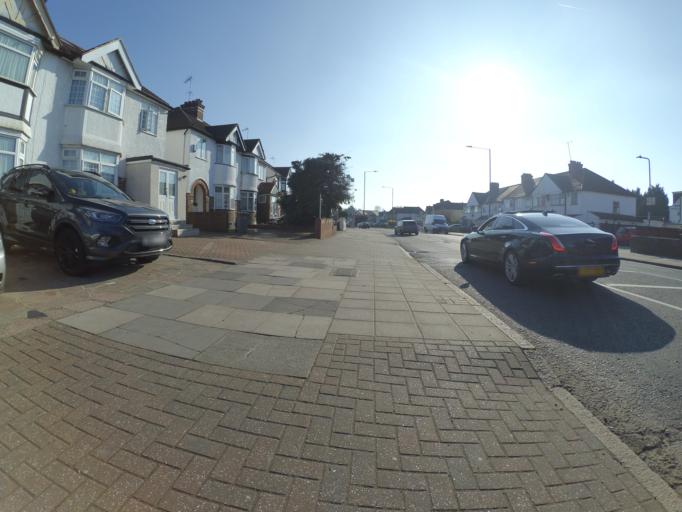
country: GB
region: England
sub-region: Greater London
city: Wembley
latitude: 51.5696
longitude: -0.2629
